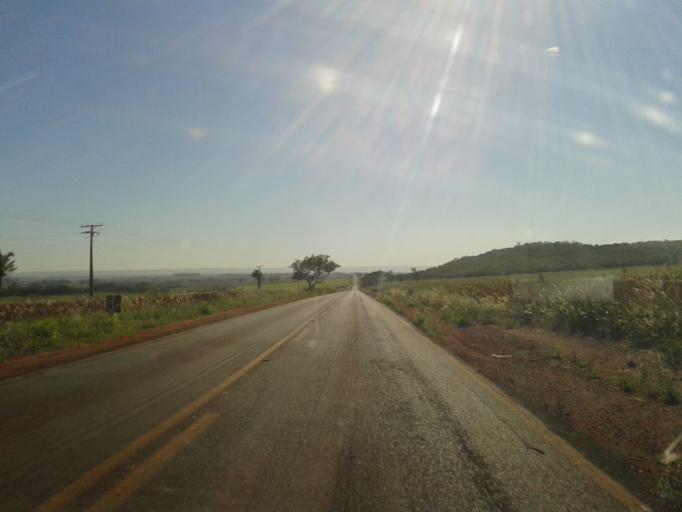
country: BR
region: Minas Gerais
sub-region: Capinopolis
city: Capinopolis
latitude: -18.6359
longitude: -49.5424
